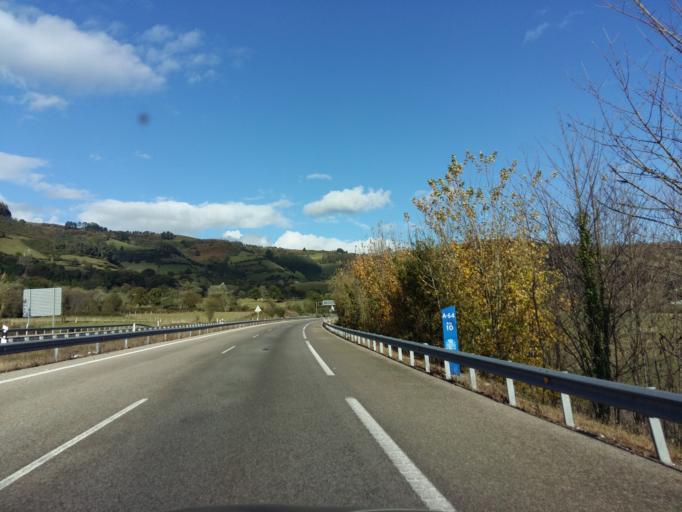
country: ES
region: Asturias
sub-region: Province of Asturias
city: Sariego
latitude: 43.4098
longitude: -5.5673
